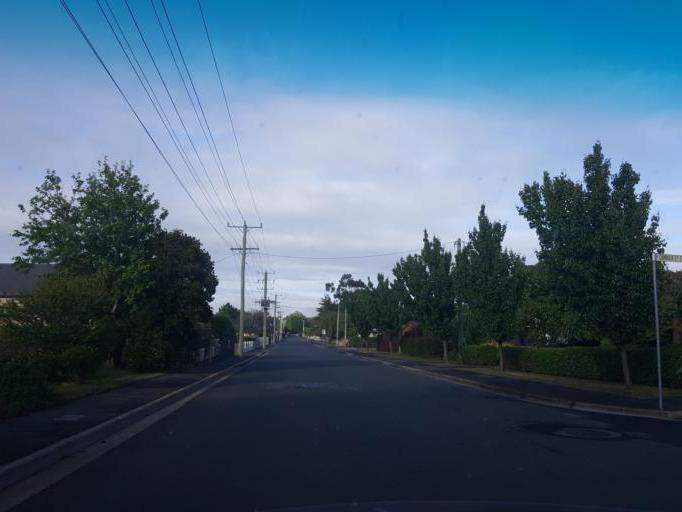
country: AU
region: Tasmania
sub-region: Northern Midlands
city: Evandale
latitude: -41.5671
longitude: 147.2503
